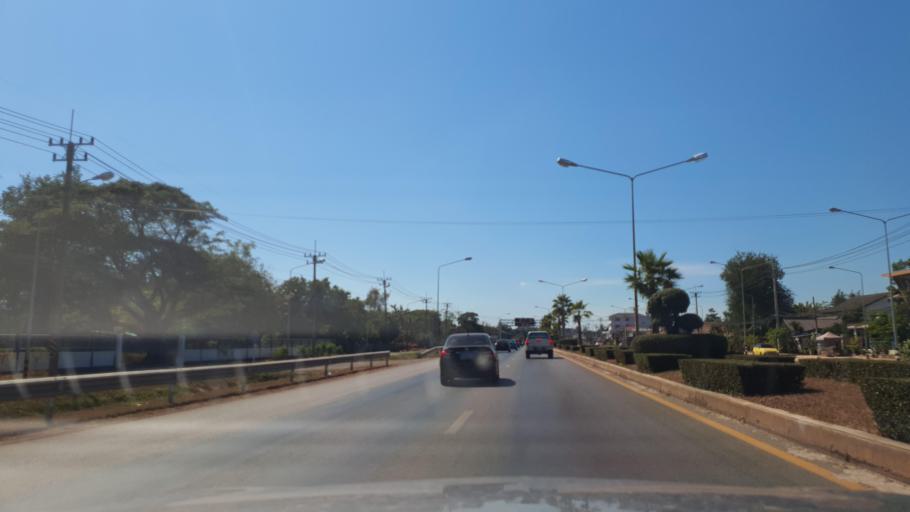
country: TH
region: Sakon Nakhon
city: Sakon Nakhon
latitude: 17.2022
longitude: 104.0997
